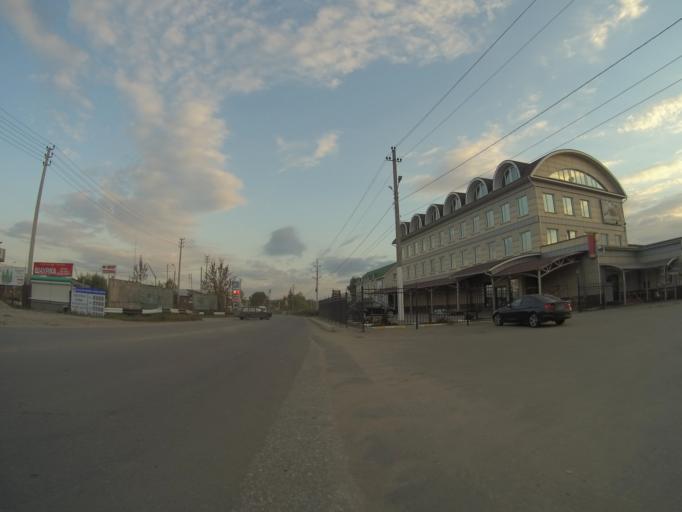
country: RU
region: Vladimir
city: Vladimir
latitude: 56.0973
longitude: 40.3488
